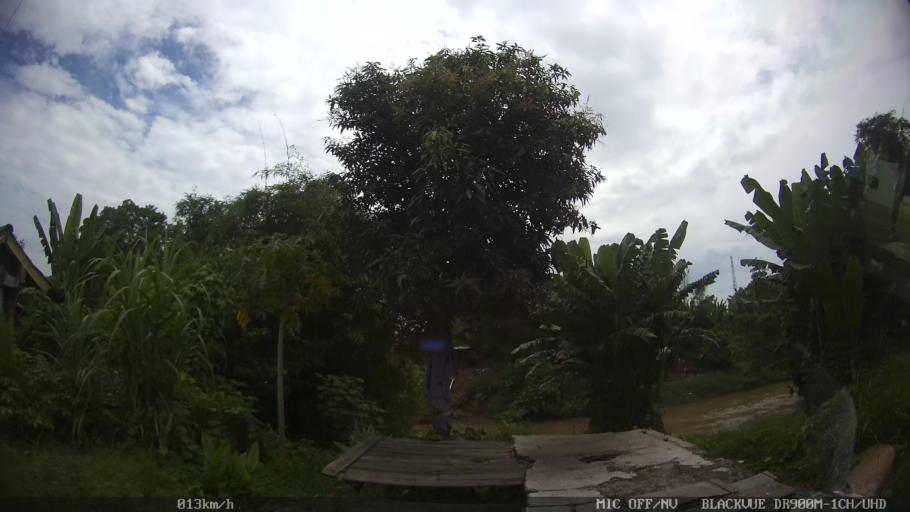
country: ID
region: North Sumatra
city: Sunggal
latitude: 3.6437
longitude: 98.5918
